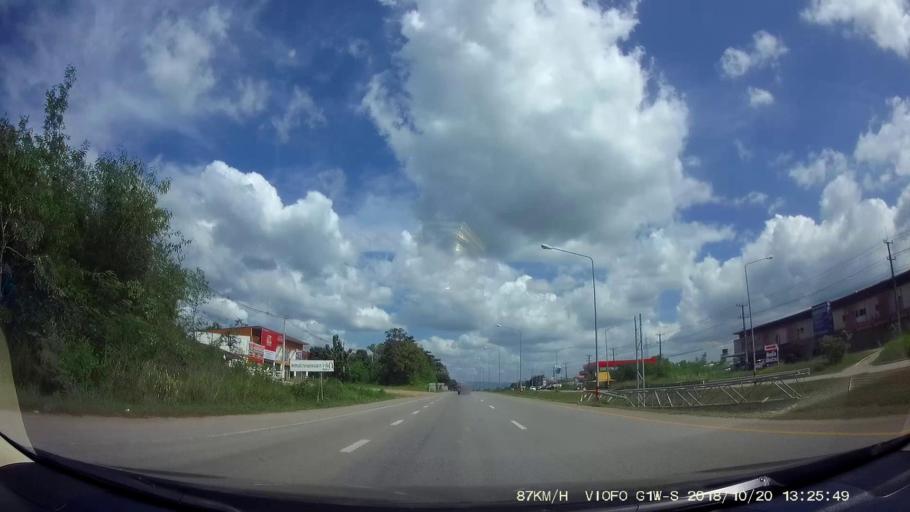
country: TH
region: Chaiyaphum
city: Khon San
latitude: 16.5945
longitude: 101.9373
